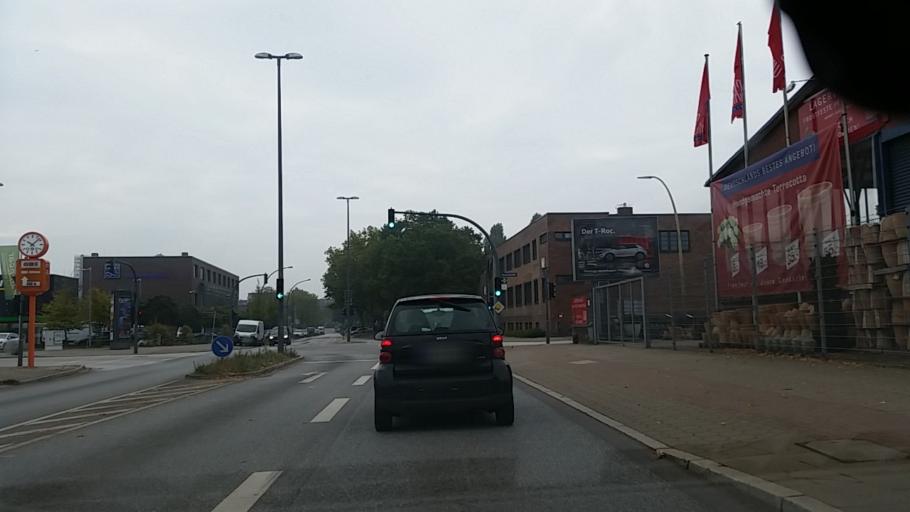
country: DE
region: Hamburg
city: Altona
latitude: 53.5680
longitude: 9.9179
